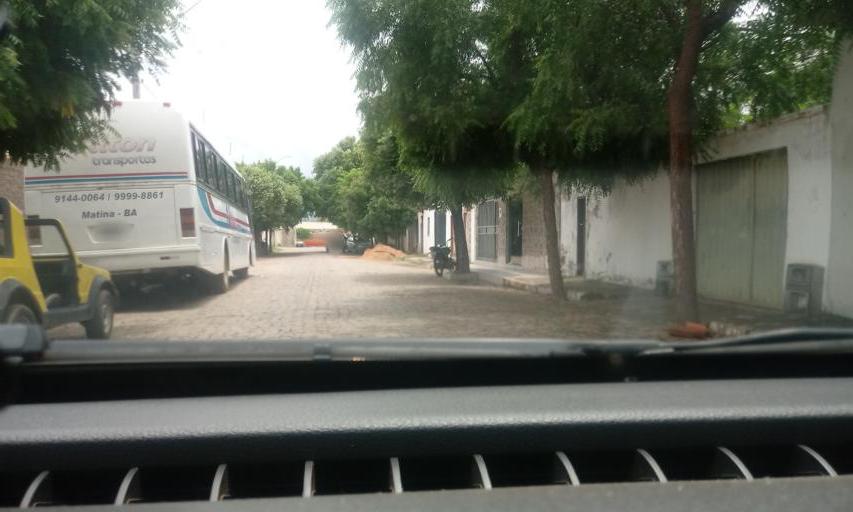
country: BR
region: Bahia
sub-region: Riacho De Santana
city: Riacho de Santana
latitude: -13.9097
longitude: -42.8438
